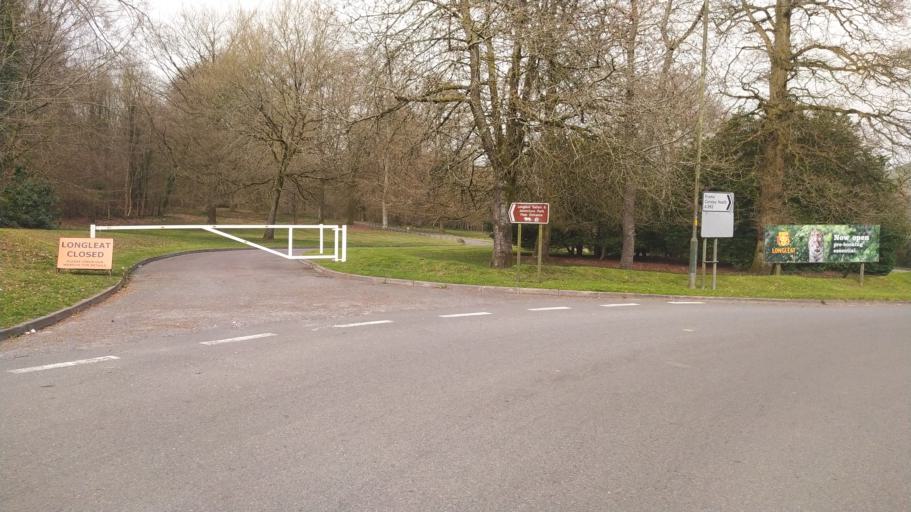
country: GB
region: England
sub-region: Wiltshire
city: Corsley
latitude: 51.1953
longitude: -2.2286
